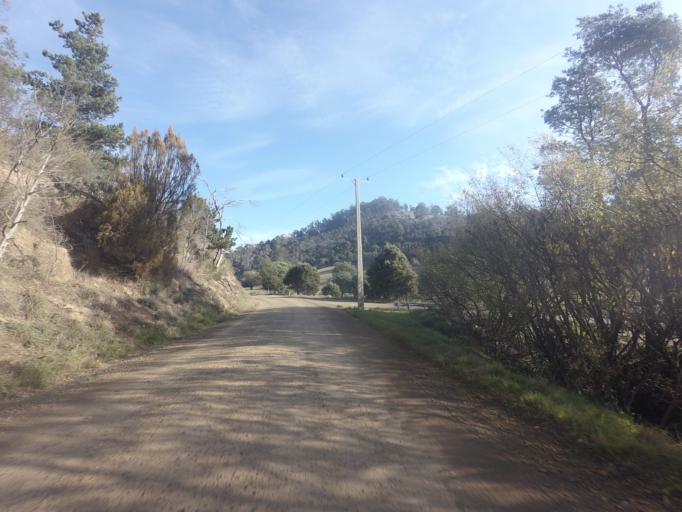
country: AU
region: Tasmania
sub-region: Sorell
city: Sorell
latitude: -42.5034
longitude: 147.4305
